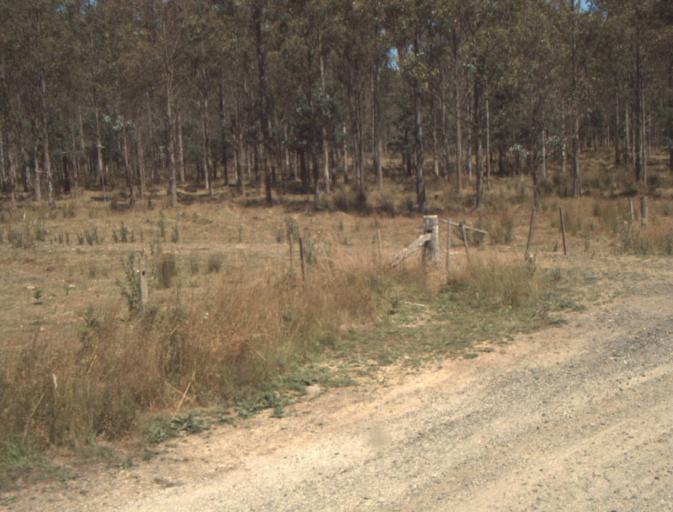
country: AU
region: Tasmania
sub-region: Dorset
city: Scottsdale
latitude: -41.3318
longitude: 147.4358
